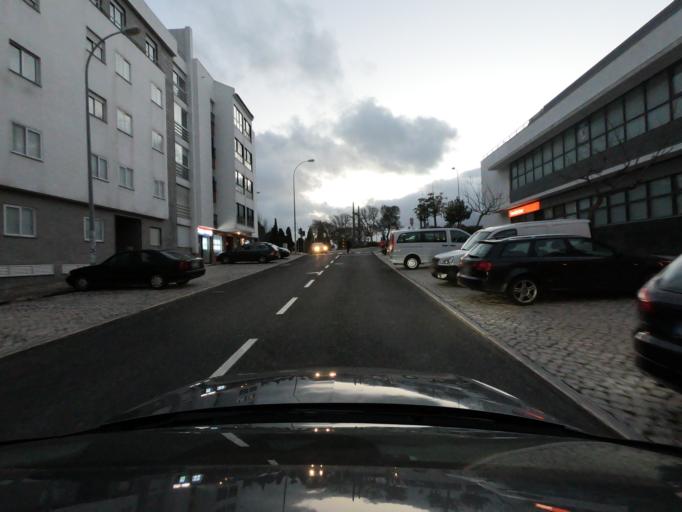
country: PT
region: Lisbon
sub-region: Oeiras
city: Oeiras
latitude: 38.6990
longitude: -9.3054
